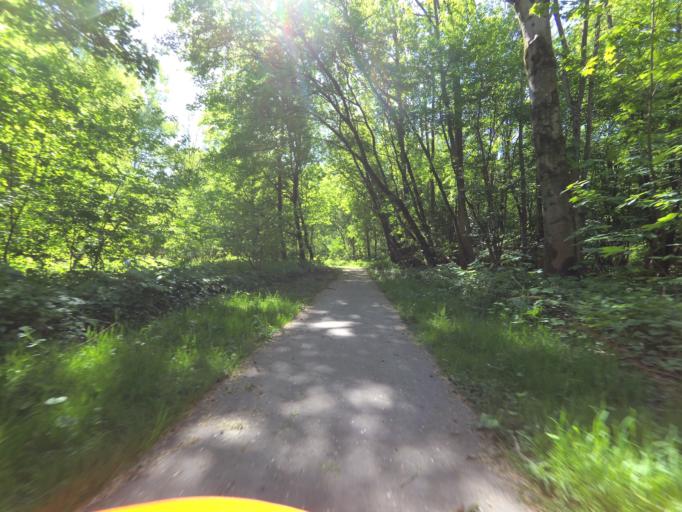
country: NL
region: Gelderland
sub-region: Gemeente Harderwijk
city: Harderwijk
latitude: 52.4022
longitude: 5.6244
